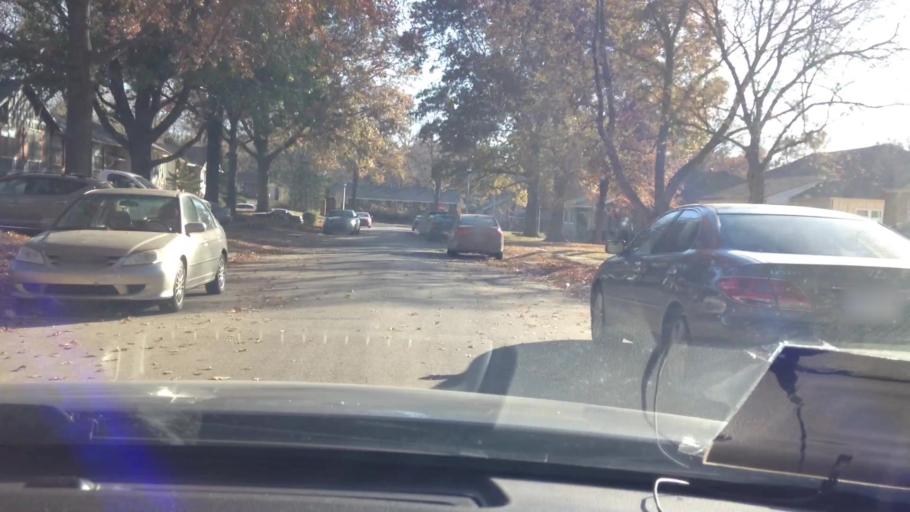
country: US
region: Kansas
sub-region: Johnson County
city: Overland Park
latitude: 38.9870
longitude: -94.6904
